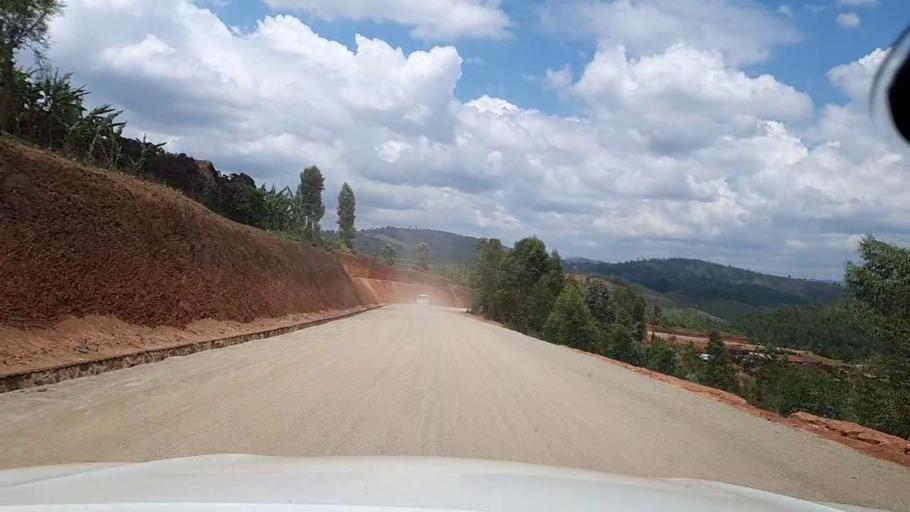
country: RW
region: Southern Province
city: Butare
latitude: -2.6961
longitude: 29.5604
